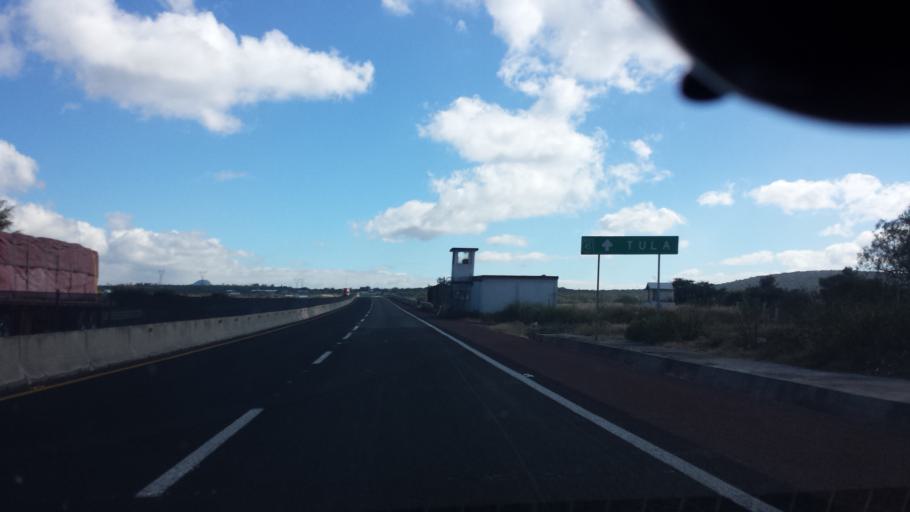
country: MX
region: Hidalgo
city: Tula de Allende
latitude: 20.0672
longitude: -99.3775
